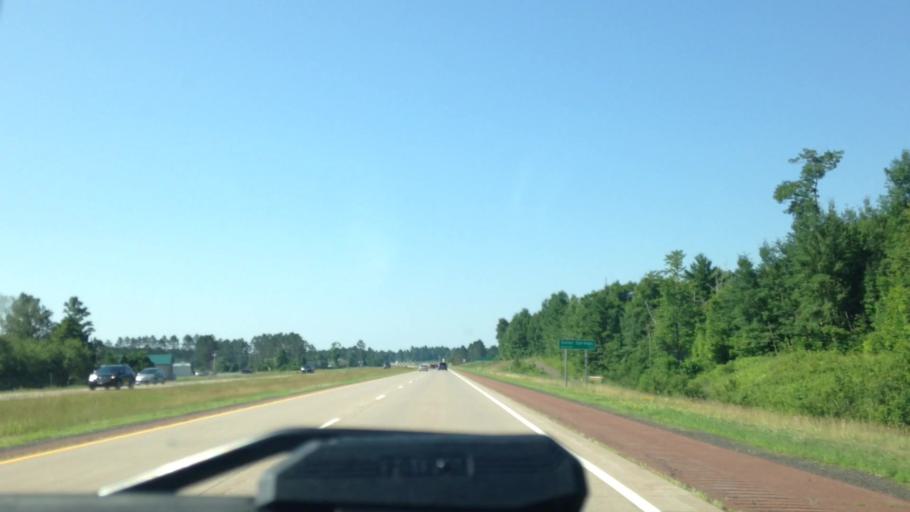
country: US
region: Wisconsin
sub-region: Douglas County
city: Lake Nebagamon
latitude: 46.3640
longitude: -91.8307
